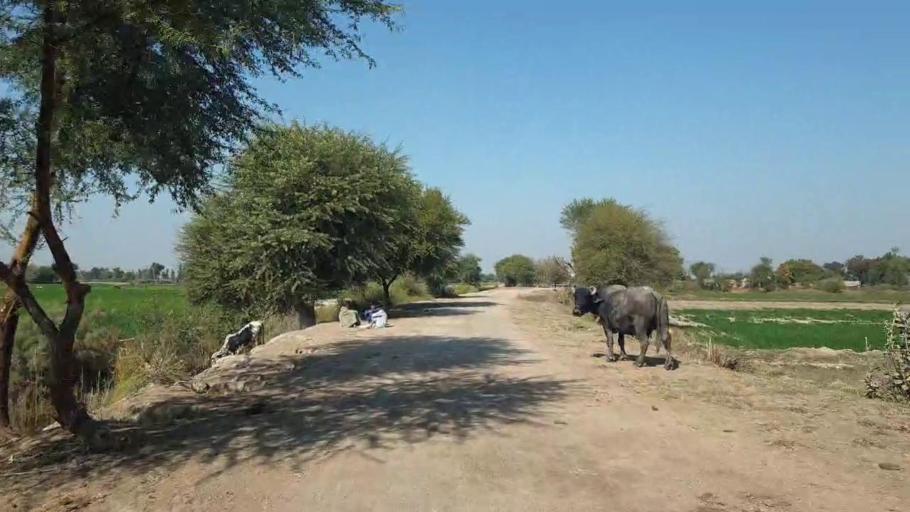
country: PK
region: Sindh
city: Shahdadpur
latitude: 25.9568
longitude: 68.6518
